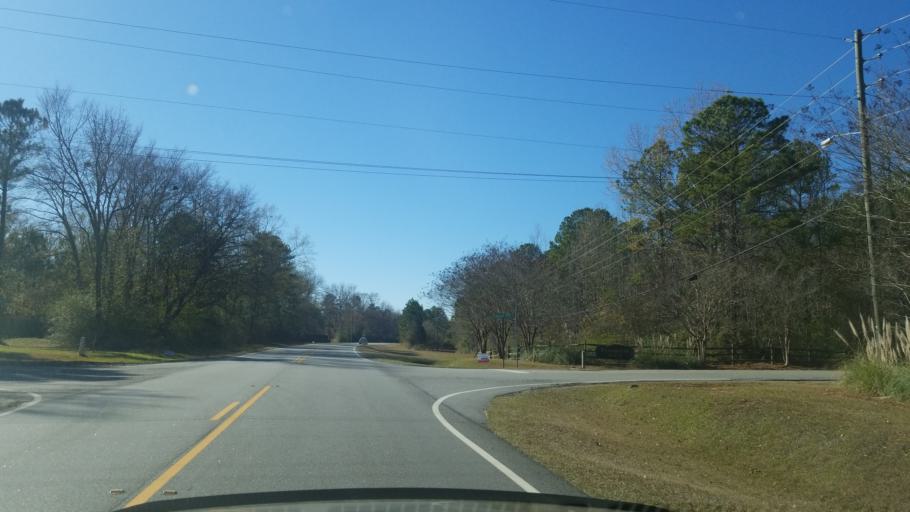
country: US
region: Georgia
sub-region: Harris County
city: Hamilton
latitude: 32.6295
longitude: -84.7694
